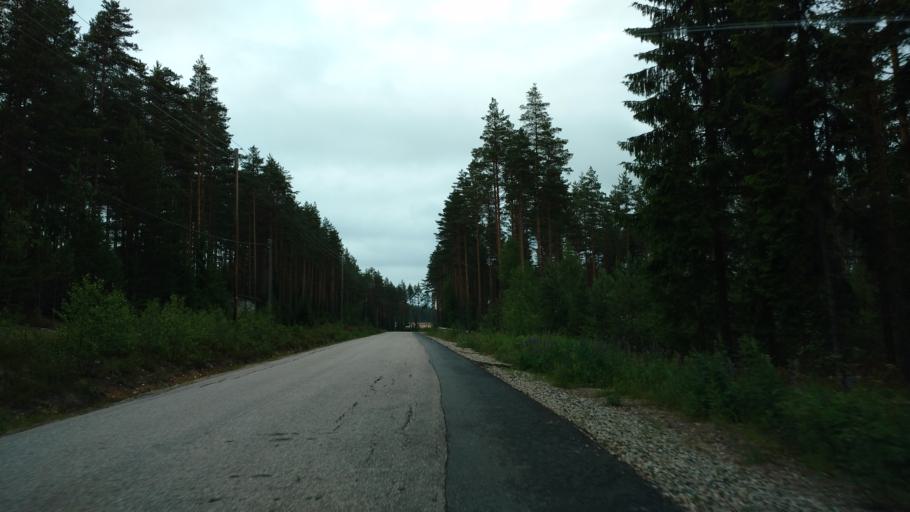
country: FI
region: Varsinais-Suomi
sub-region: Salo
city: Kiikala
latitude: 60.4318
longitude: 23.5988
